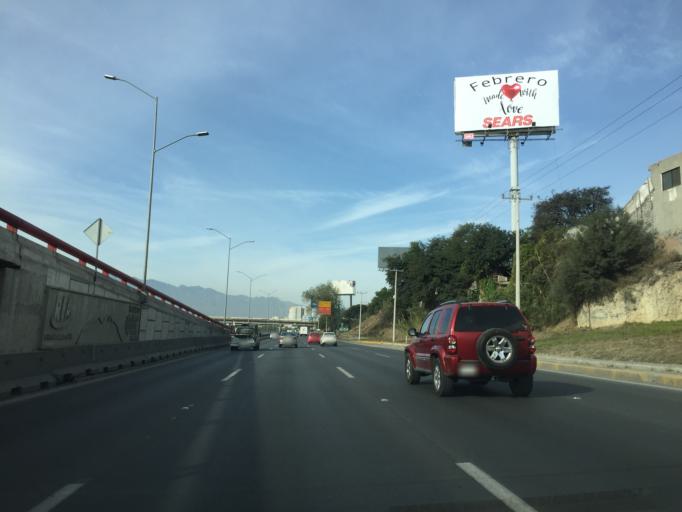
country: MX
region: Nuevo Leon
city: Guadalupe
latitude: 25.6942
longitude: -100.2263
